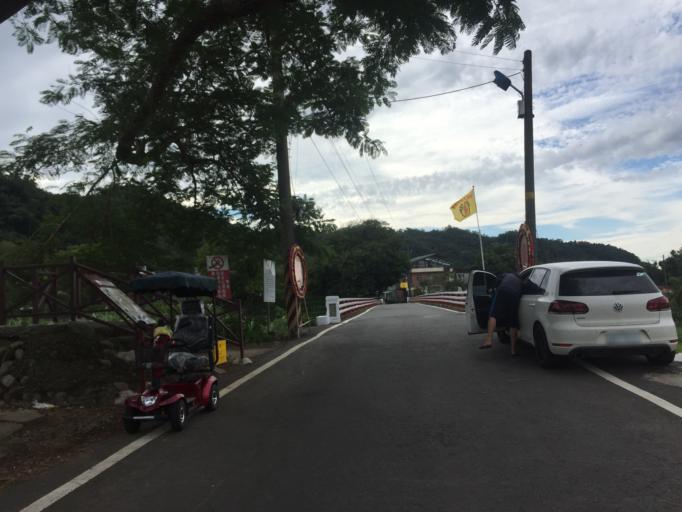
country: TW
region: Taiwan
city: Daxi
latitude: 24.7887
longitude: 121.1721
